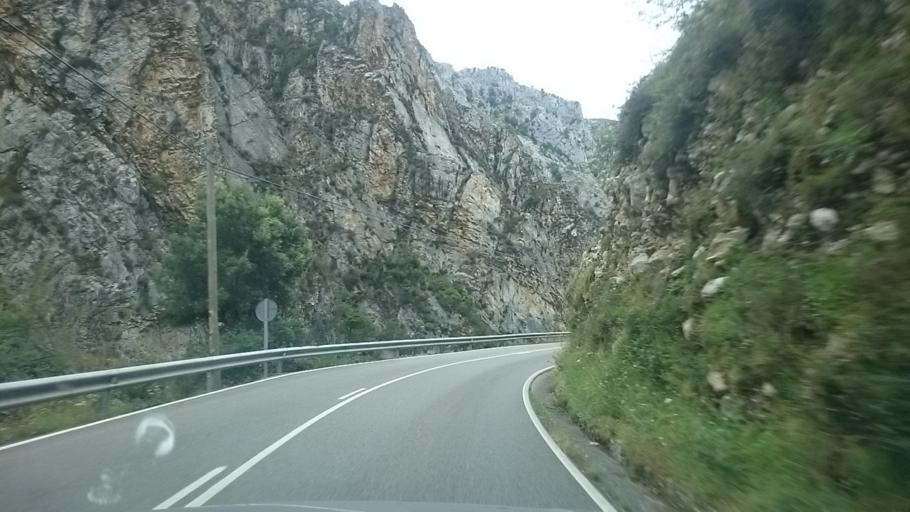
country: ES
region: Asturias
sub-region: Province of Asturias
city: Carrena
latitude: 43.2782
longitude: -4.8344
